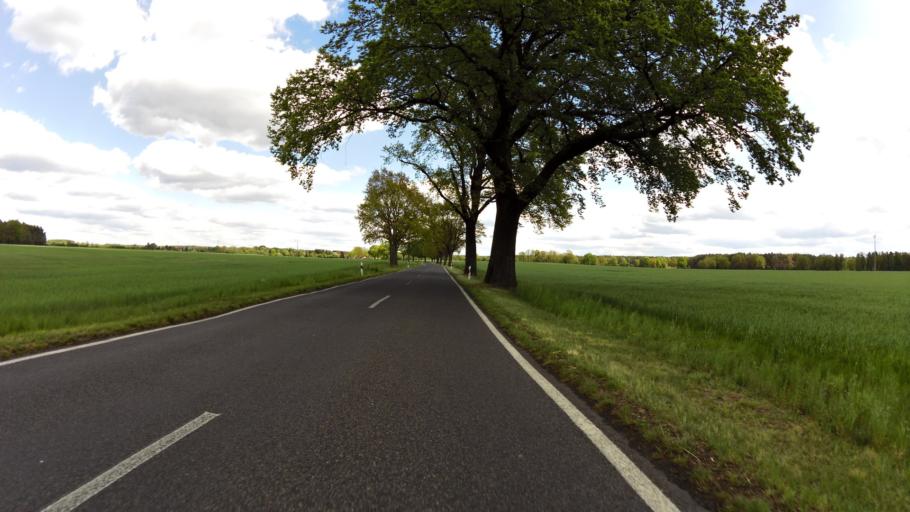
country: DE
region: Brandenburg
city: Wendisch Rietz
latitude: 52.1678
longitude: 14.0622
